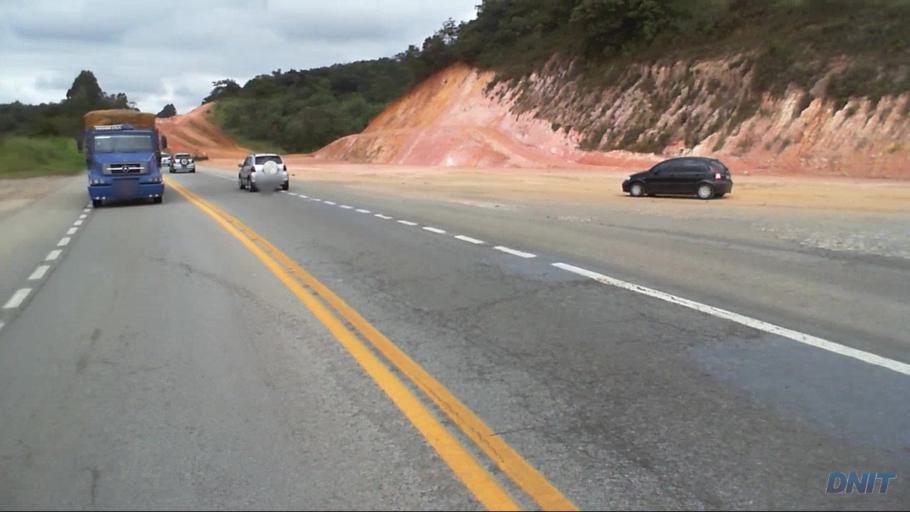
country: BR
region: Minas Gerais
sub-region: Caete
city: Caete
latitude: -19.7414
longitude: -43.5552
